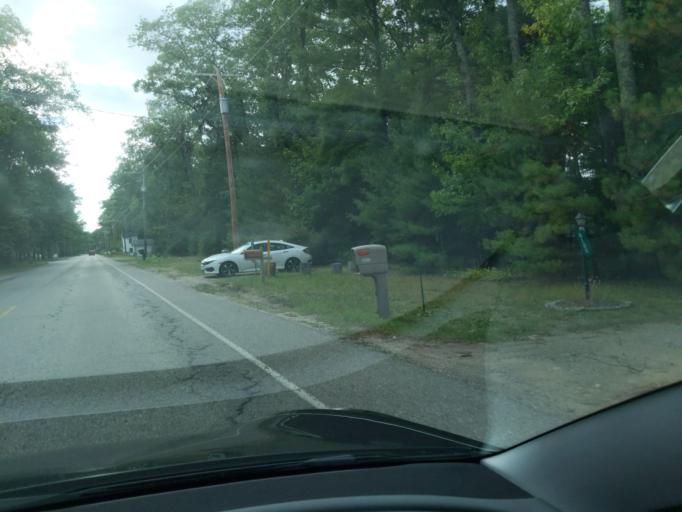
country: US
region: Michigan
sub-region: Kalkaska County
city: Rapid City
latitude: 44.8577
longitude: -85.2963
